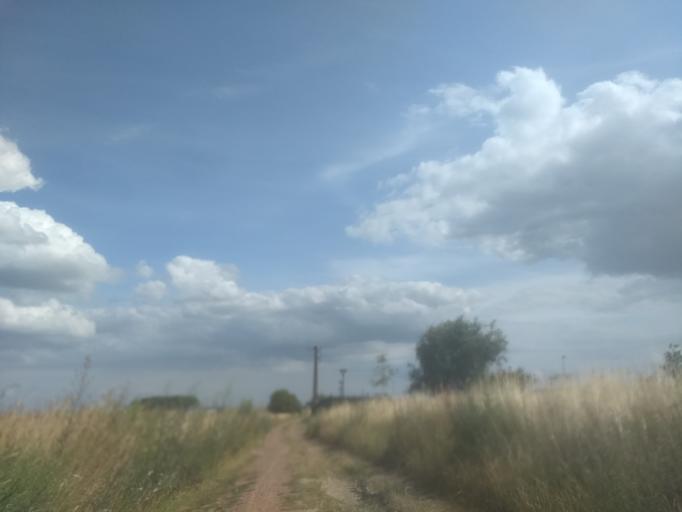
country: FR
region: Nord-Pas-de-Calais
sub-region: Departement du Pas-de-Calais
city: Beaurains
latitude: 50.2722
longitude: 2.7989
